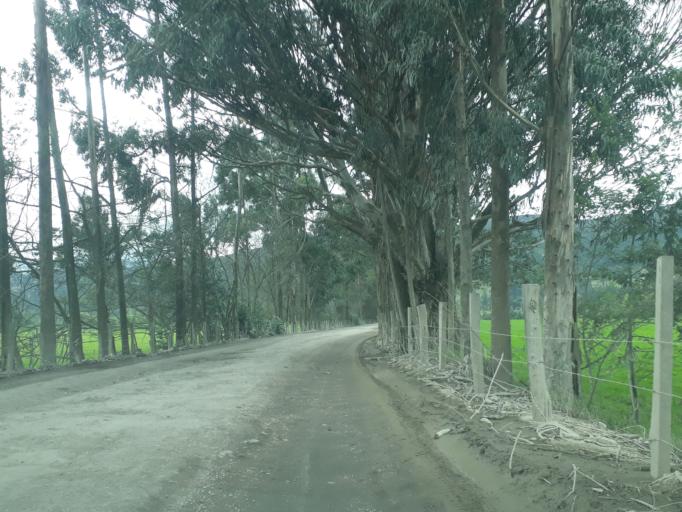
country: CO
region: Cundinamarca
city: Lenguazaque
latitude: 5.3342
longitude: -73.7102
